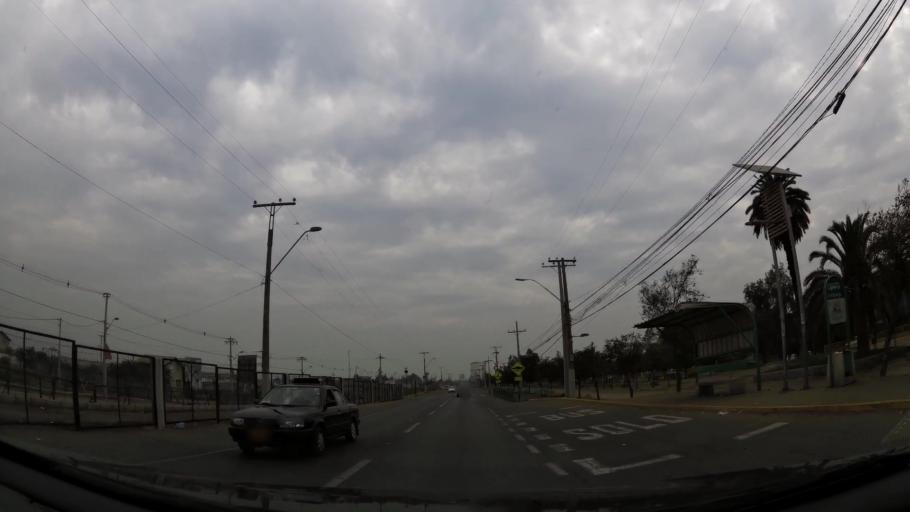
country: CL
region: Santiago Metropolitan
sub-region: Provincia de Chacabuco
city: Chicureo Abajo
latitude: -33.1946
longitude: -70.6669
